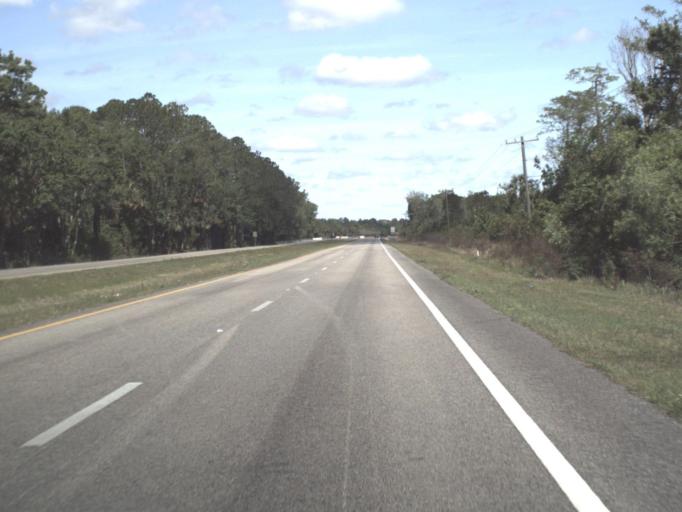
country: US
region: Florida
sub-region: Flagler County
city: Bunnell
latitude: 29.4484
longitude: -81.2425
